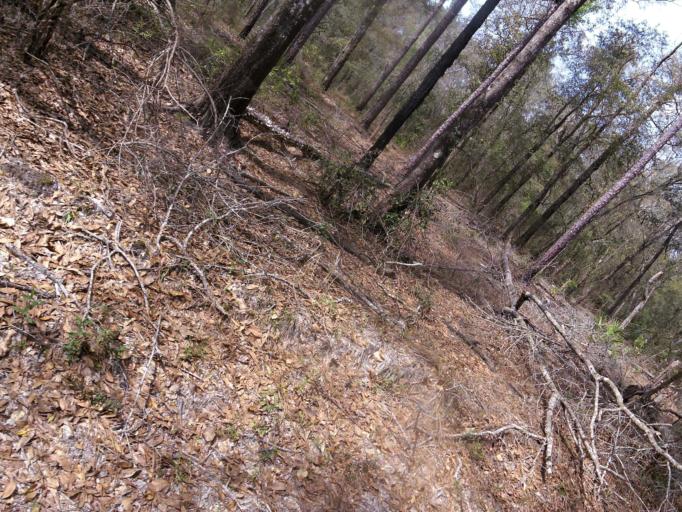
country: US
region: Florida
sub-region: Clay County
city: Middleburg
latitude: 30.1239
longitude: -81.8845
